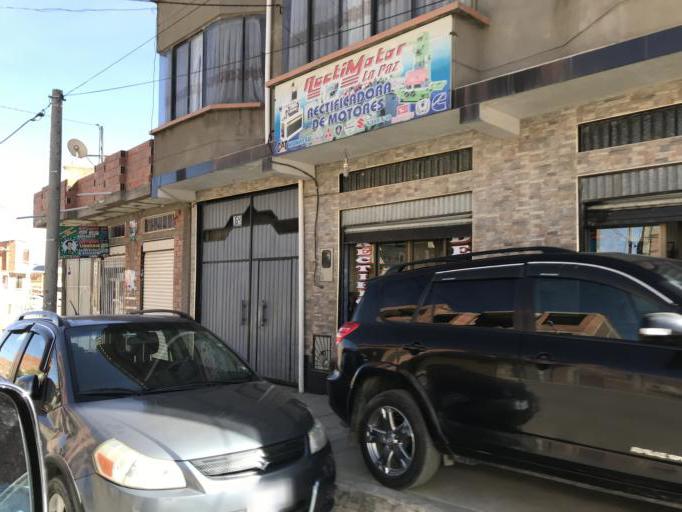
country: BO
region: La Paz
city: La Paz
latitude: -16.4867
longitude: -68.1802
